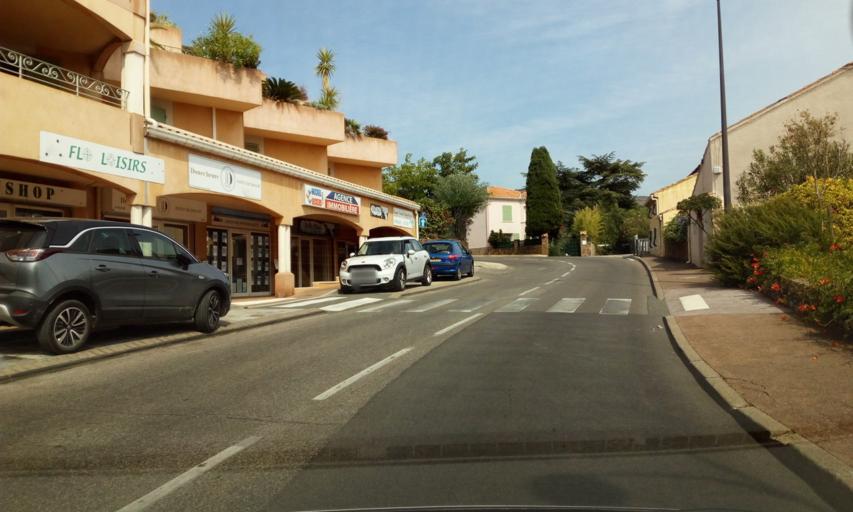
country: FR
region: Provence-Alpes-Cote d'Azur
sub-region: Departement du Var
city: Bormes-les-Mimosas
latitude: 43.1446
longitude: 6.3383
